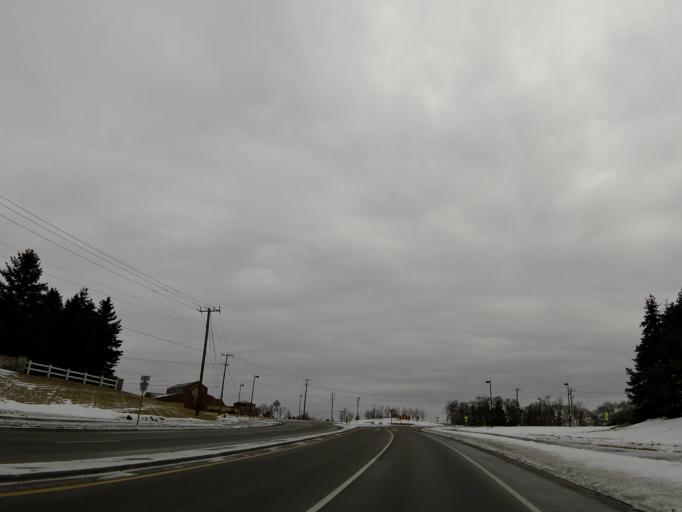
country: US
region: Minnesota
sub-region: Washington County
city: Woodbury
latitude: 44.8920
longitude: -92.9035
